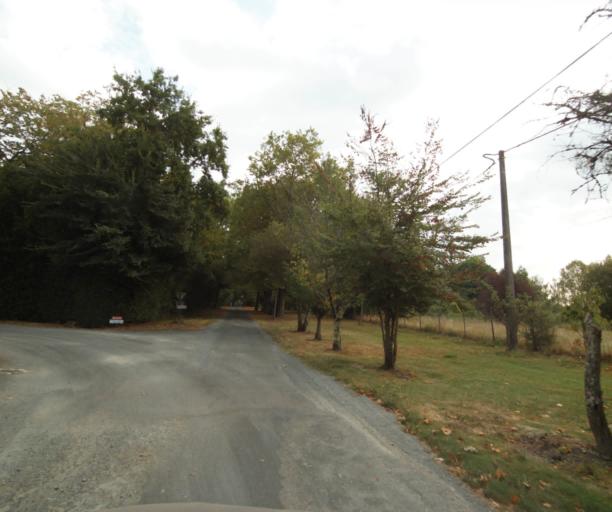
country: FR
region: Aquitaine
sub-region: Departement de la Gironde
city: Creon
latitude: 44.7795
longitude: -0.3585
